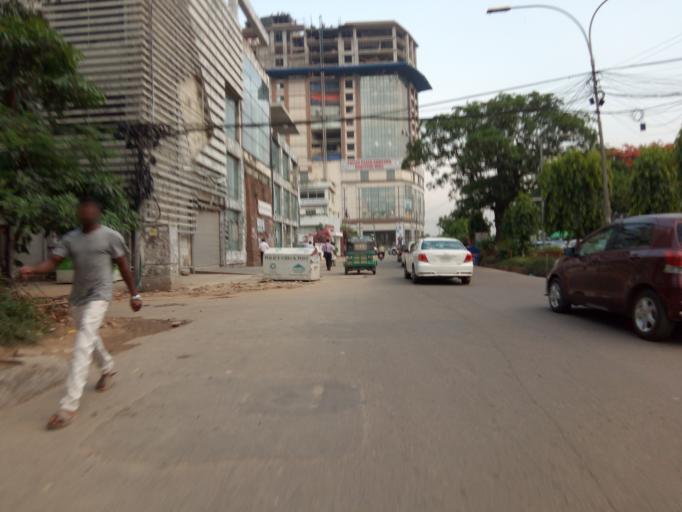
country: BD
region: Dhaka
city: Paltan
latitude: 23.7743
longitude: 90.4162
